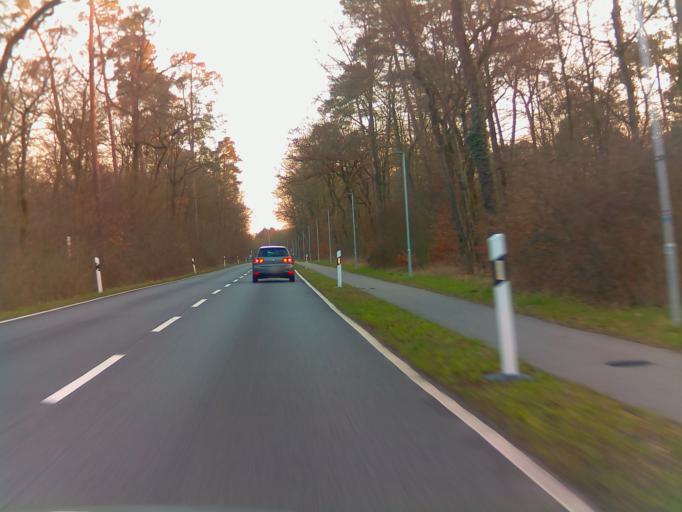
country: DE
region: Baden-Wuerttemberg
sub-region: Karlsruhe Region
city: Walldorf
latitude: 49.3192
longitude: 8.6443
